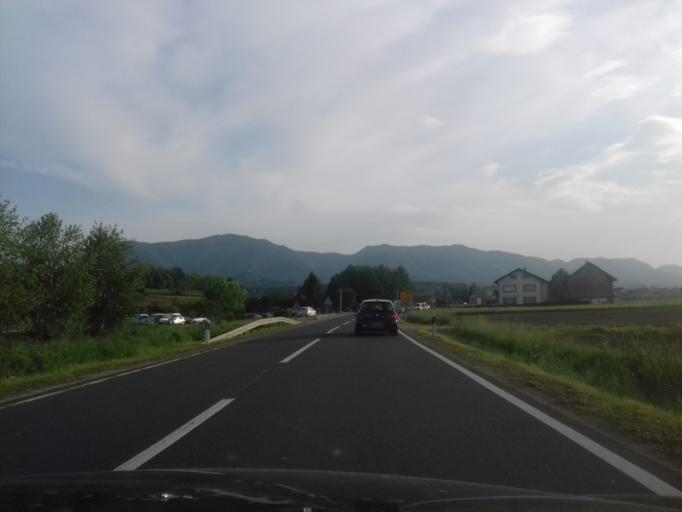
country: HR
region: Varazdinska
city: Ivanec
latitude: 46.2377
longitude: 16.1574
